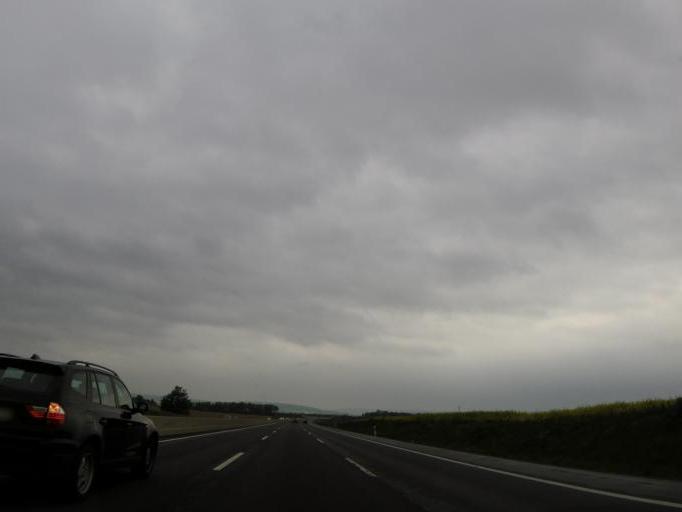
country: DE
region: Lower Saxony
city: Haverlah
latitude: 52.0259
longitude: 10.1709
